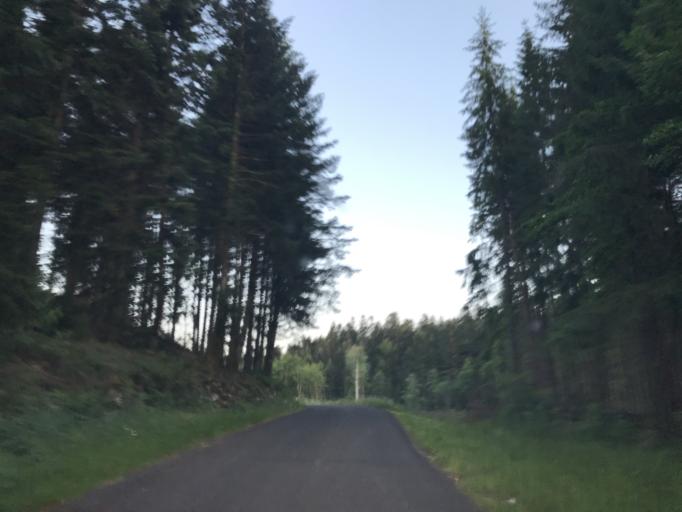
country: FR
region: Rhone-Alpes
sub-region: Departement de la Loire
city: Noiretable
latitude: 45.7645
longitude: 3.7093
